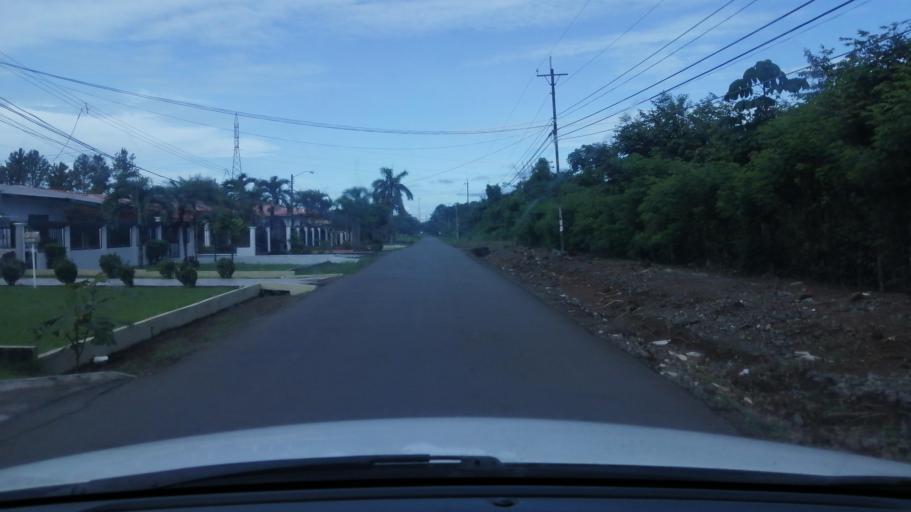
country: PA
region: Chiriqui
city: El Quiteno
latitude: 8.4666
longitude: -82.4142
